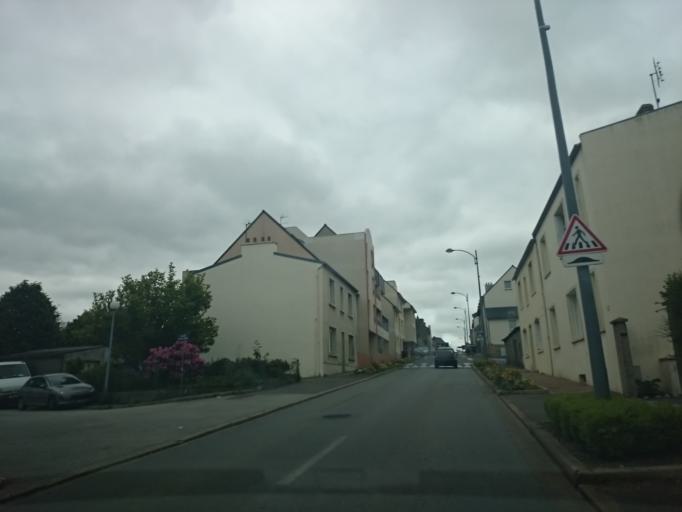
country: FR
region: Brittany
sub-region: Departement du Finistere
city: Gouesnou
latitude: 48.4482
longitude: -4.4651
